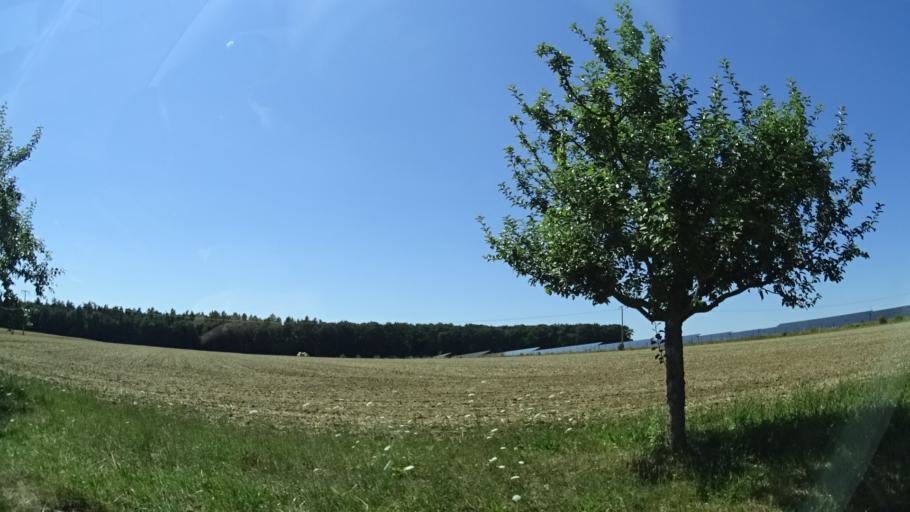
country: DE
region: Bavaria
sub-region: Regierungsbezirk Unterfranken
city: Gadheim
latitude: 49.8382
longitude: 9.9066
